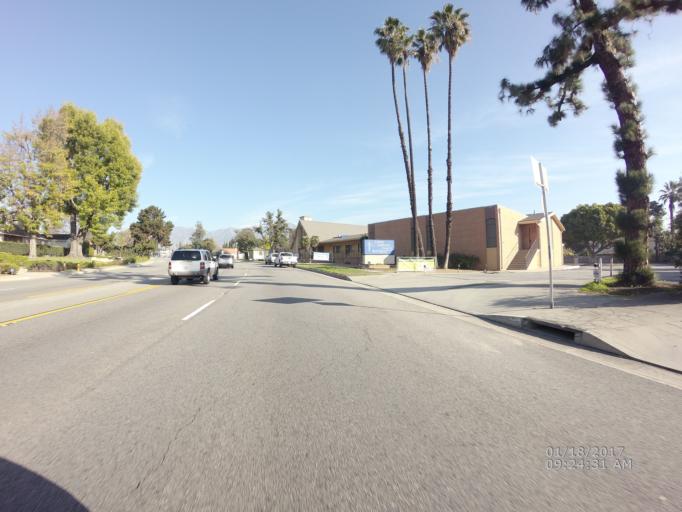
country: US
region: California
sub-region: Los Angeles County
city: San Marino
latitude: 34.1235
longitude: -118.0903
